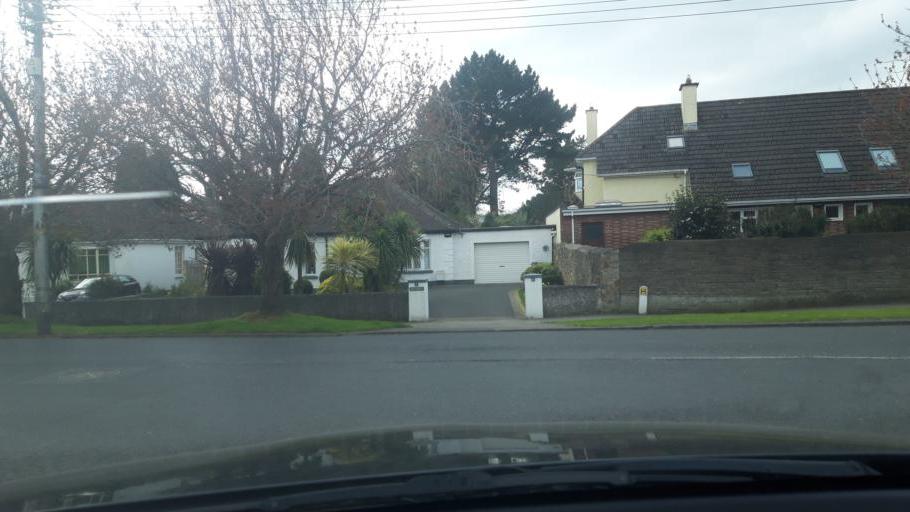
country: IE
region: Leinster
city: Dundrum
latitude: 53.2984
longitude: -6.2683
